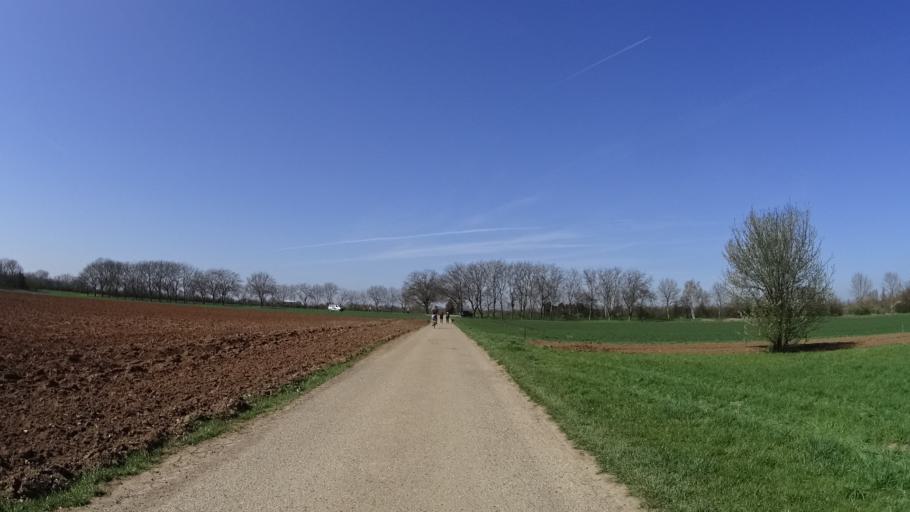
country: DE
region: Baden-Wuerttemberg
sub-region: Karlsruhe Region
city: Dossenheim
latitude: 49.4428
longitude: 8.6545
